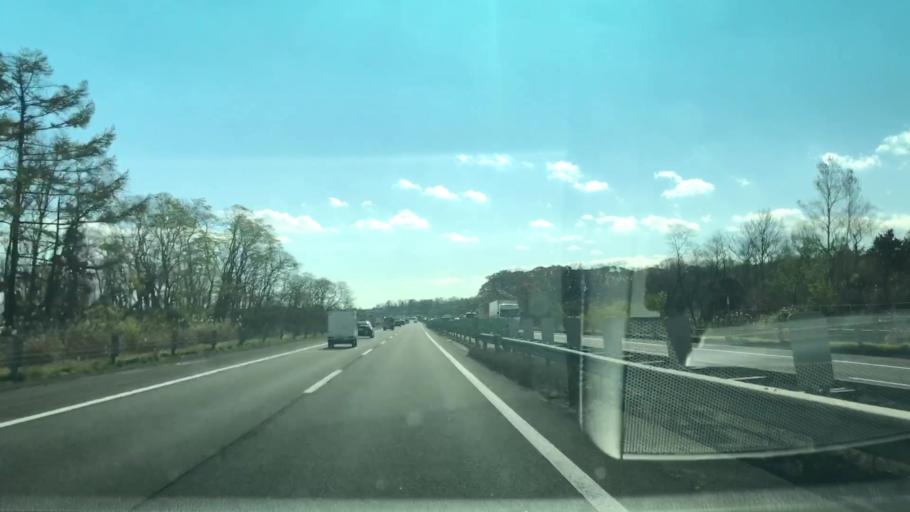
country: JP
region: Hokkaido
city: Kitahiroshima
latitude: 42.8980
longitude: 141.5502
